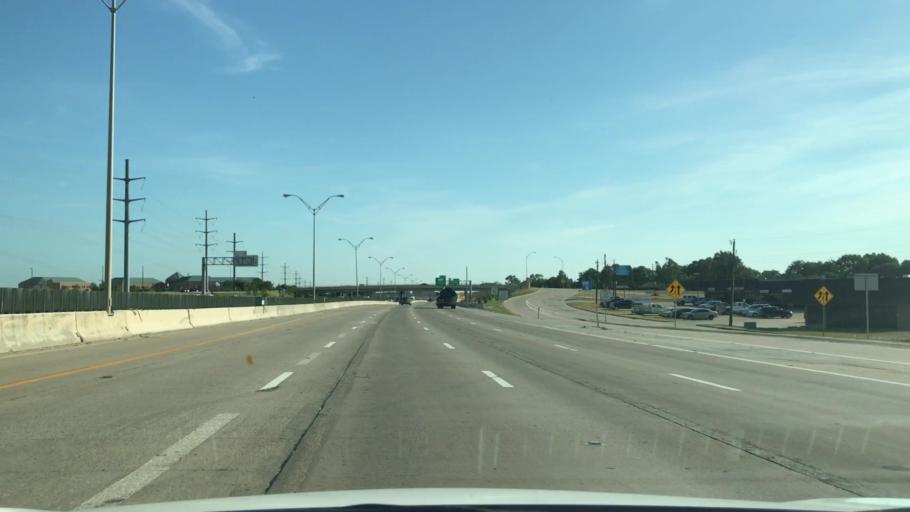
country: US
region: Texas
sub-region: Collin County
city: Allen
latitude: 33.1094
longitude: -96.6741
